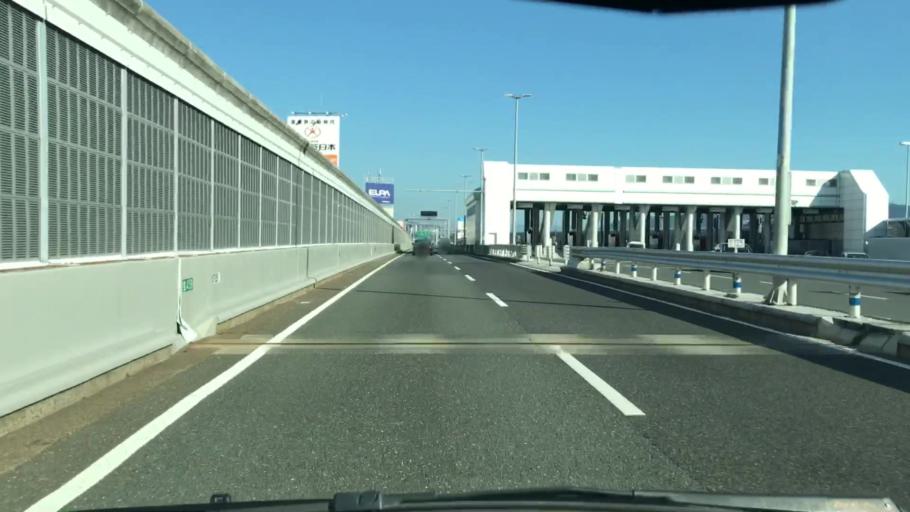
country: JP
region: Osaka
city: Toyonaka
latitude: 34.7834
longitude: 135.4523
